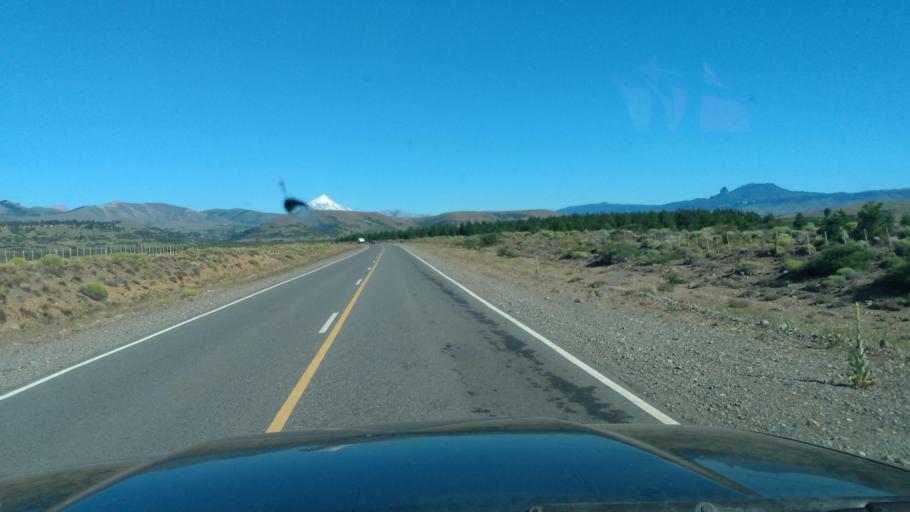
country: AR
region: Neuquen
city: Junin de los Andes
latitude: -39.8782
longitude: -71.1667
